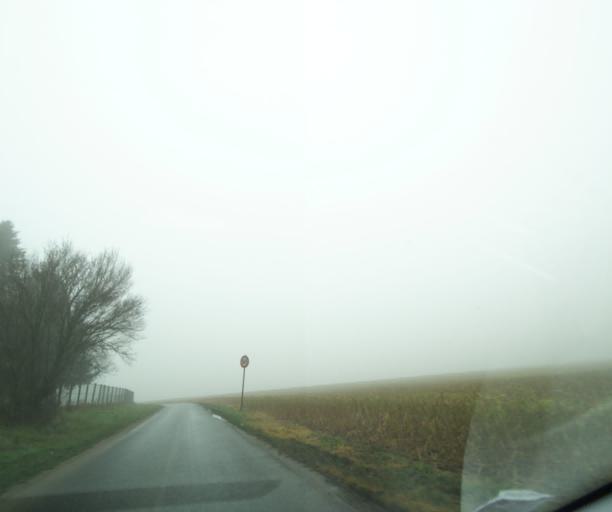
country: FR
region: Ile-de-France
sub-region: Departement de Seine-et-Marne
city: Longperrier
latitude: 49.0463
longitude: 2.6654
